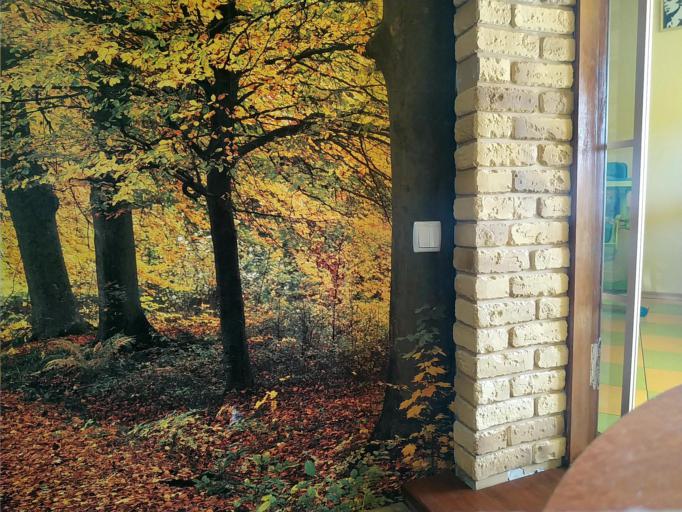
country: RU
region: Smolensk
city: Katyn'
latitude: 54.9930
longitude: 31.7466
